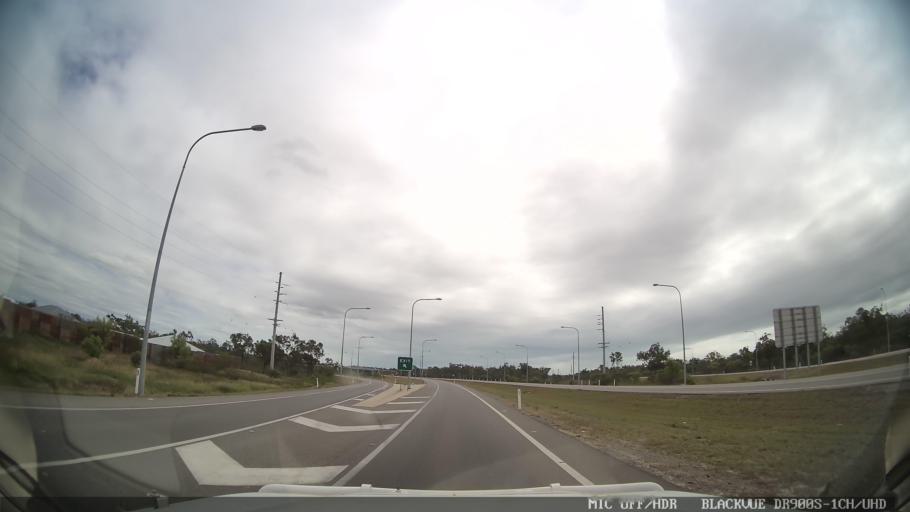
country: AU
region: Queensland
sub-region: Townsville
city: Bohle Plains
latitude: -19.3010
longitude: 146.6956
